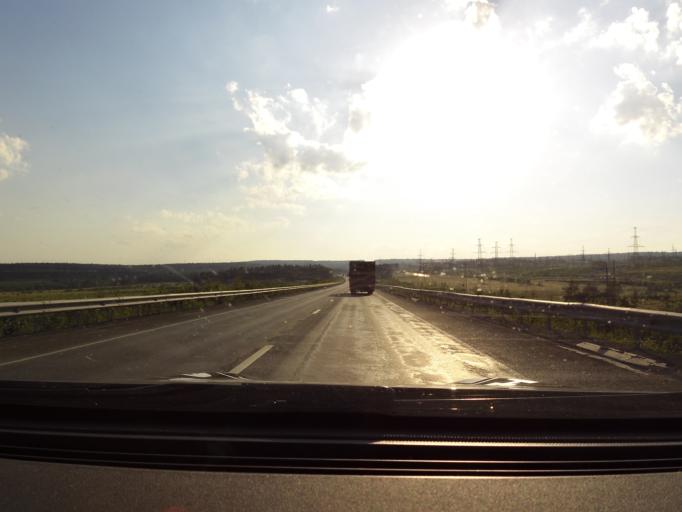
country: RU
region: Sverdlovsk
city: Revda
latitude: 56.8268
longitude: 59.9005
